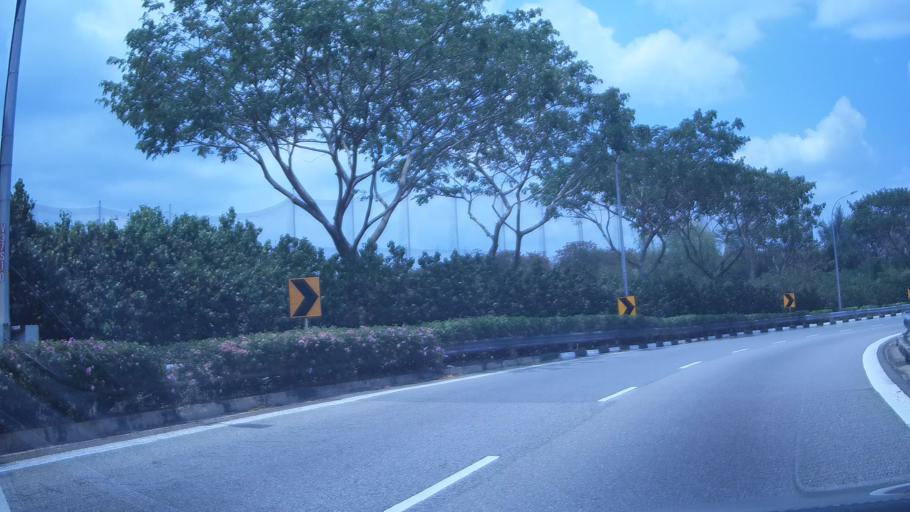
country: SG
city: Singapore
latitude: 1.2938
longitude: 103.8749
